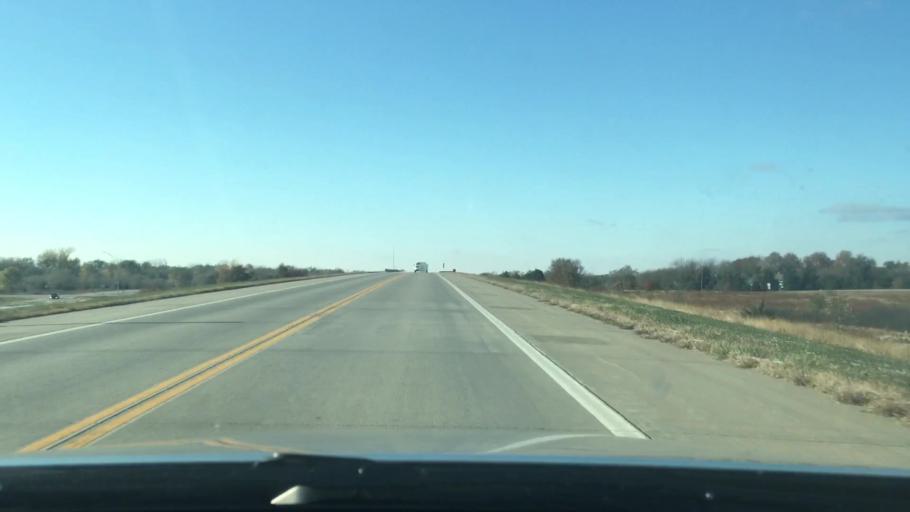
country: US
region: Kansas
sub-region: Reno County
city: Hutchinson
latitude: 38.0898
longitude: -97.9946
